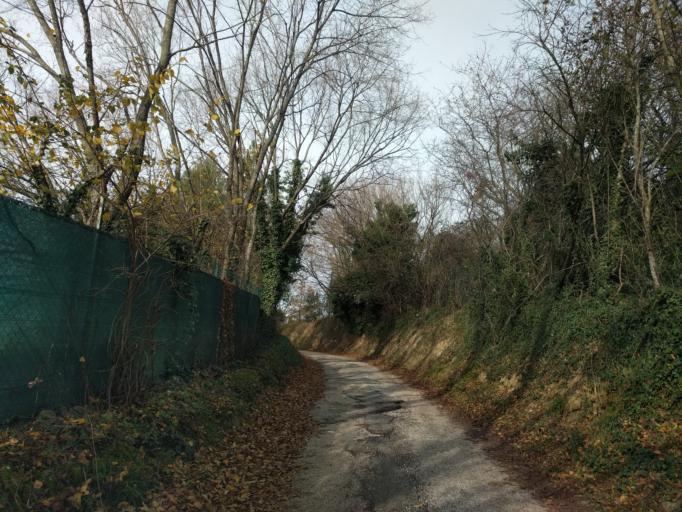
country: IT
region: The Marches
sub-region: Provincia di Pesaro e Urbino
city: Centinarola
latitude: 43.8168
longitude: 12.9728
